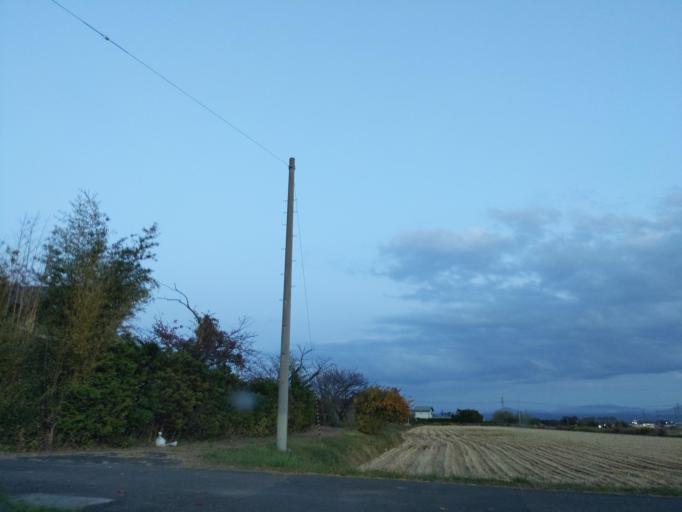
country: JP
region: Fukushima
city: Koriyama
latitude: 37.4629
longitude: 140.3198
